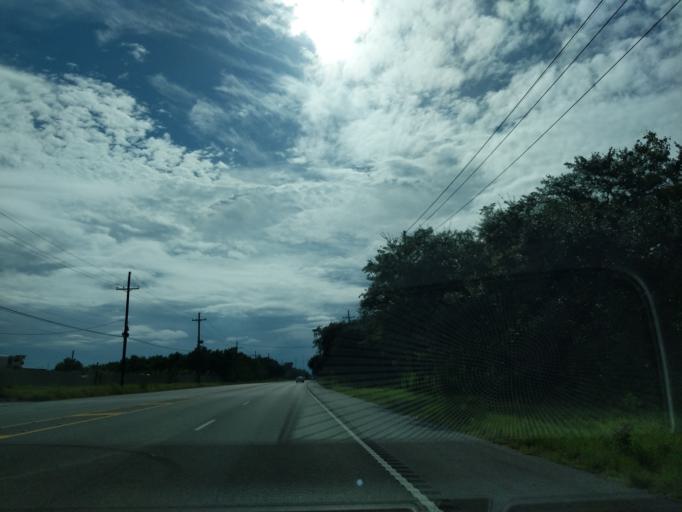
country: US
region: Louisiana
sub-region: Saint Bernard Parish
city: Meraux
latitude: 30.0563
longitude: -89.8735
